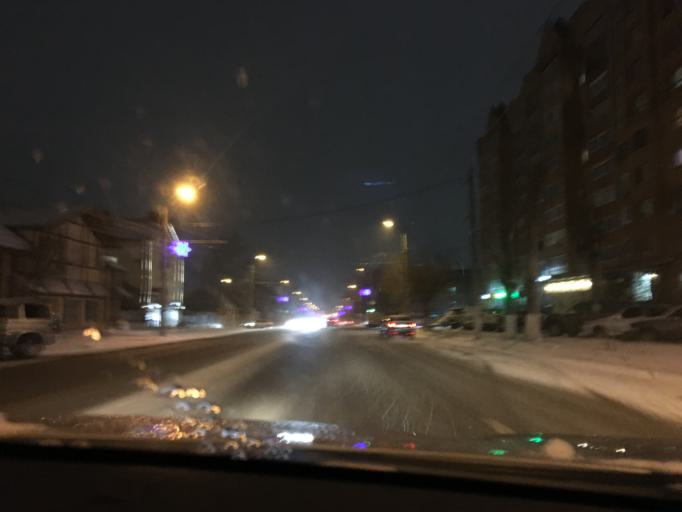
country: RU
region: Tula
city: Mendeleyevskiy
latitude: 54.1755
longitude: 37.5746
